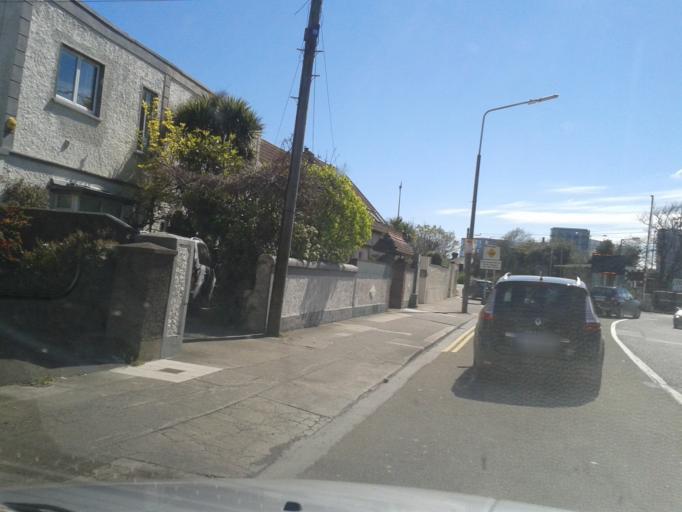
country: IE
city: Booterstown
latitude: 53.3169
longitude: -6.2050
